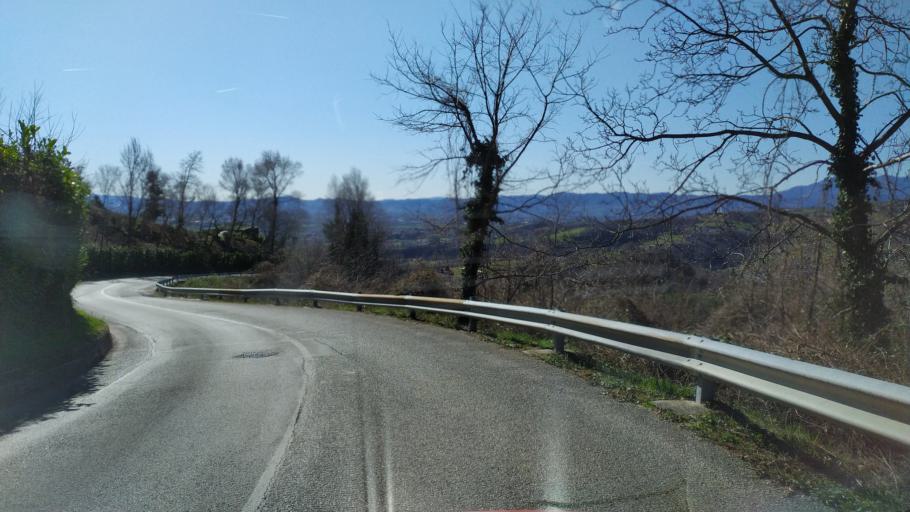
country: IT
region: Veneto
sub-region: Provincia di Vicenza
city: Lugo di Vicenza
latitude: 45.7589
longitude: 11.5346
